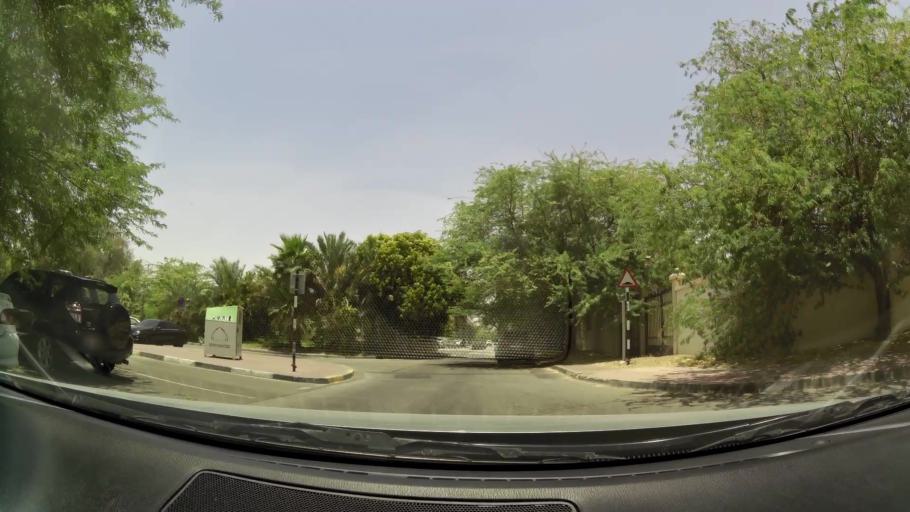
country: OM
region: Al Buraimi
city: Al Buraymi
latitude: 24.2612
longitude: 55.7389
